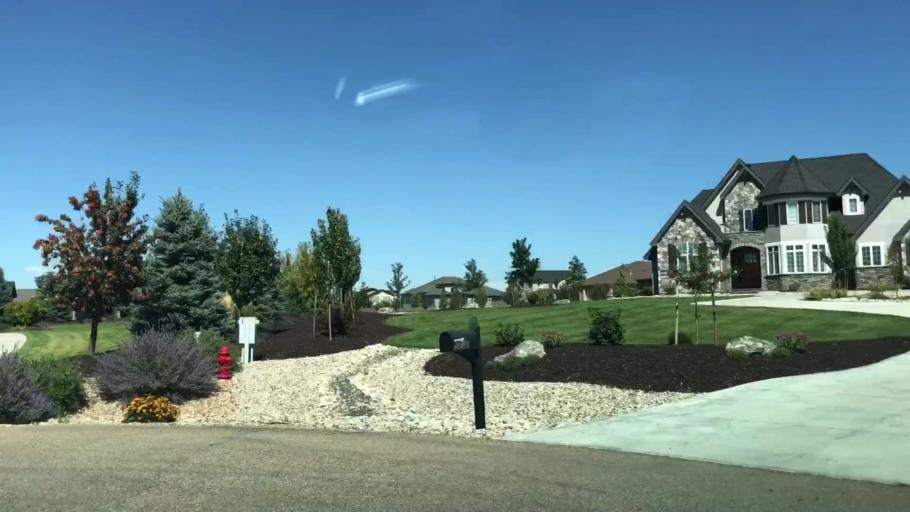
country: US
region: Colorado
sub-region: Weld County
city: Windsor
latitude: 40.4496
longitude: -104.9578
